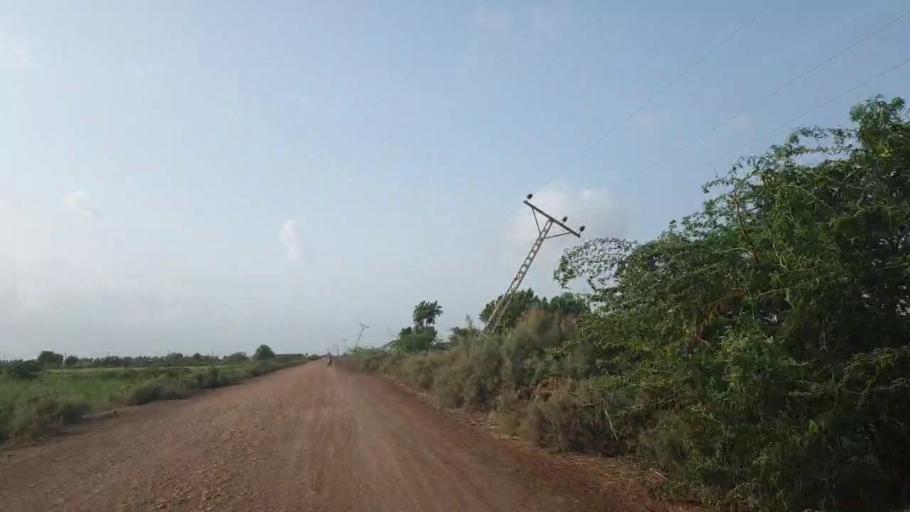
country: PK
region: Sindh
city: Tando Bago
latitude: 24.6484
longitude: 69.1119
